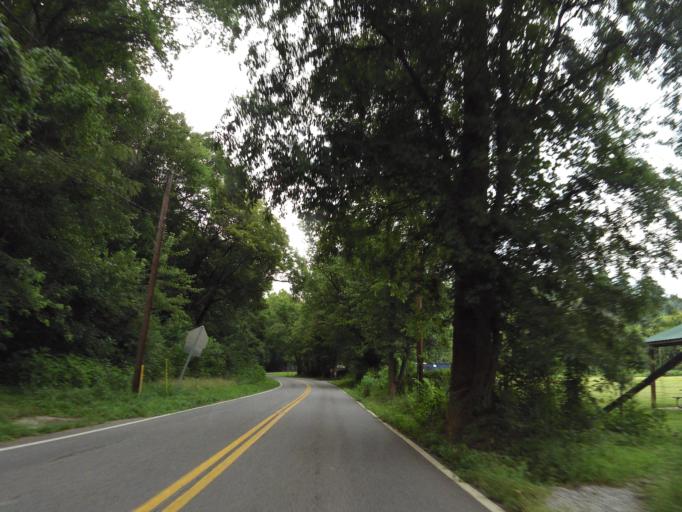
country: US
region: Tennessee
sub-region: Anderson County
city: Rocky Top
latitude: 36.1793
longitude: -84.1824
